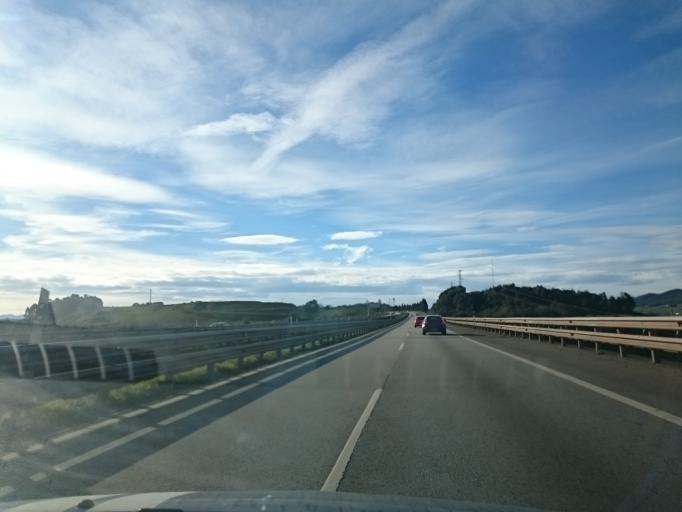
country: ES
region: Asturias
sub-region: Province of Asturias
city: Natahoyo
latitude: 43.5163
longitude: -5.7265
